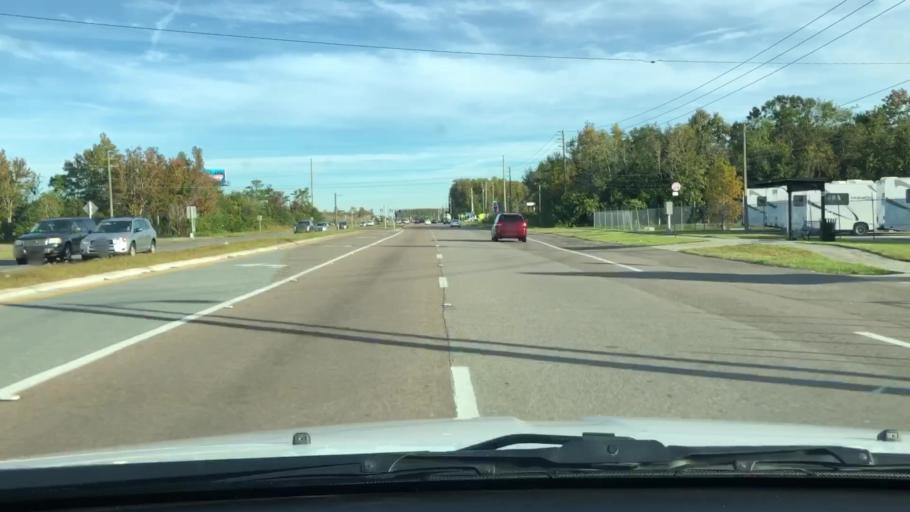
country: US
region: Florida
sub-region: Osceola County
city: Kissimmee
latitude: 28.3339
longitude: -81.4037
